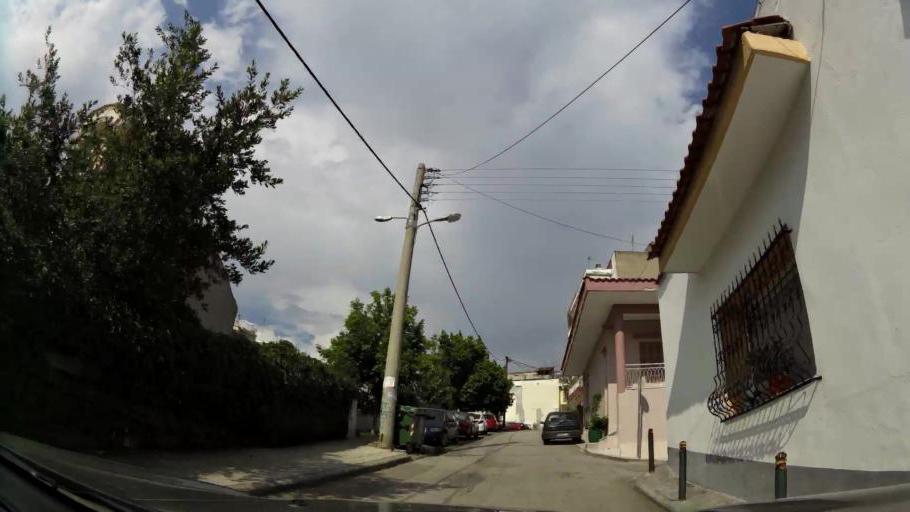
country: GR
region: Central Macedonia
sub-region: Nomos Thessalonikis
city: Polichni
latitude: 40.6611
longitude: 22.9497
